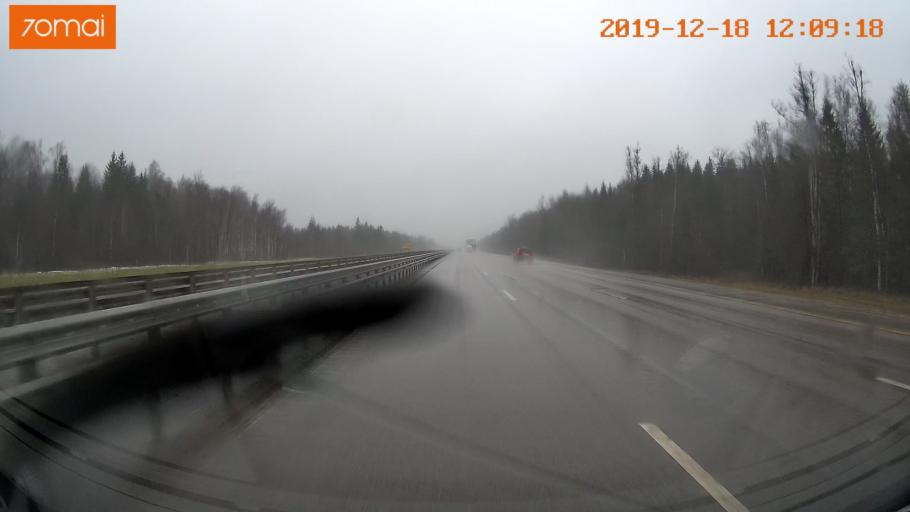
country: RU
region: Moskovskaya
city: Kostrovo
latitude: 55.9078
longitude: 36.6179
